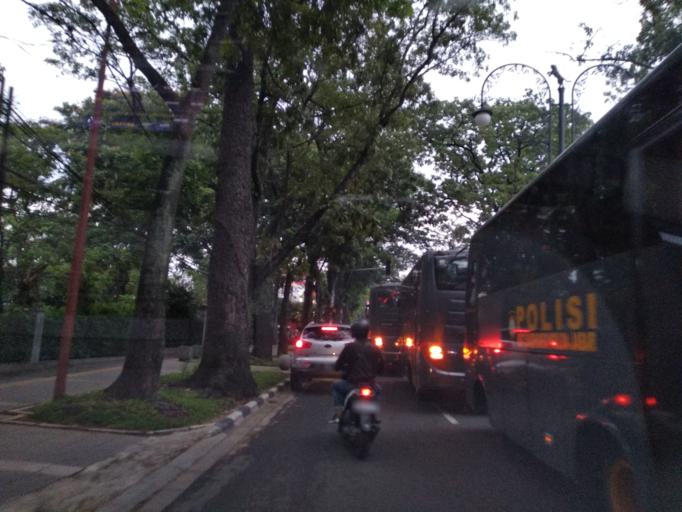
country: ID
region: West Java
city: Bandung
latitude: -6.9034
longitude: 107.6112
